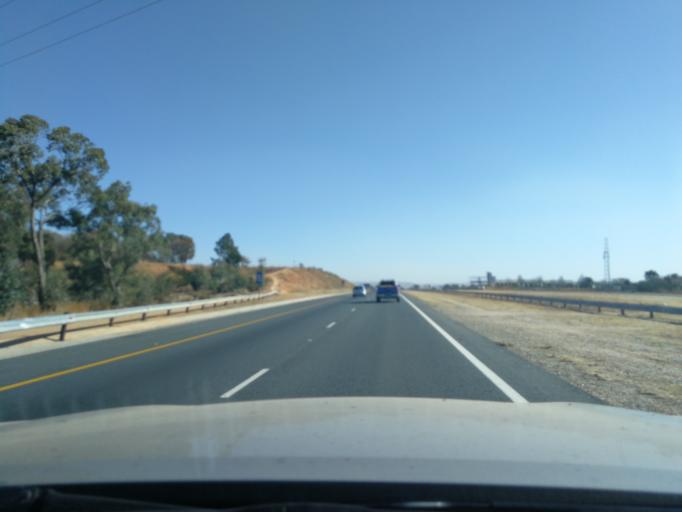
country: ZA
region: Gauteng
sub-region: West Rand District Municipality
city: Muldersdriseloop
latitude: -26.0156
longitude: 27.8723
